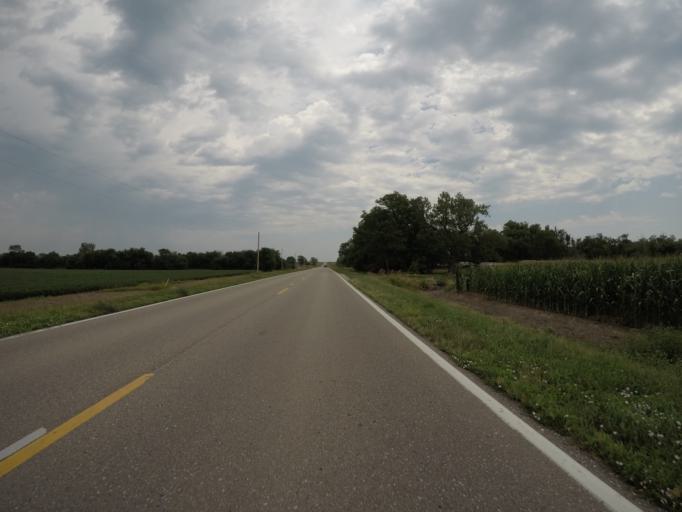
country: US
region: Nebraska
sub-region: Hall County
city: Wood River
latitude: 40.6114
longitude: -98.5970
